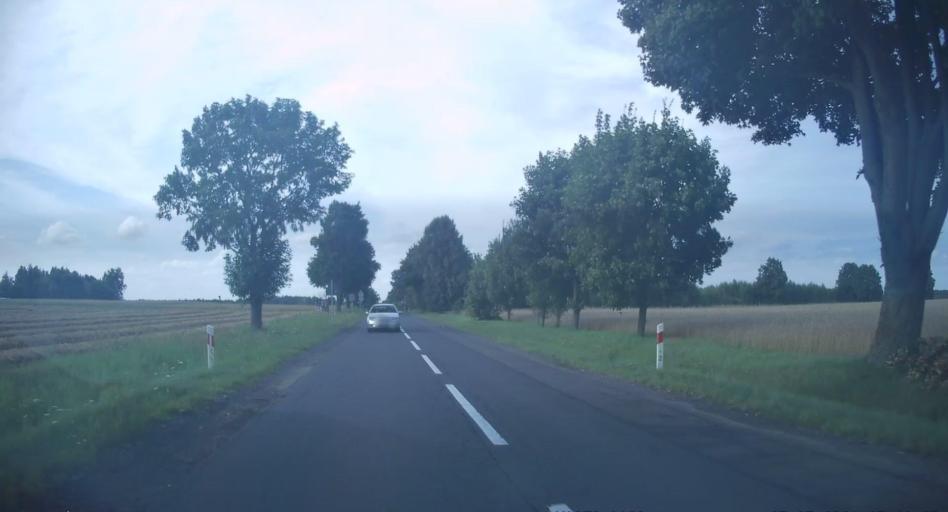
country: PL
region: Lodz Voivodeship
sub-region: Powiat rawski
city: Rawa Mazowiecka
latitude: 51.6930
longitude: 20.2666
